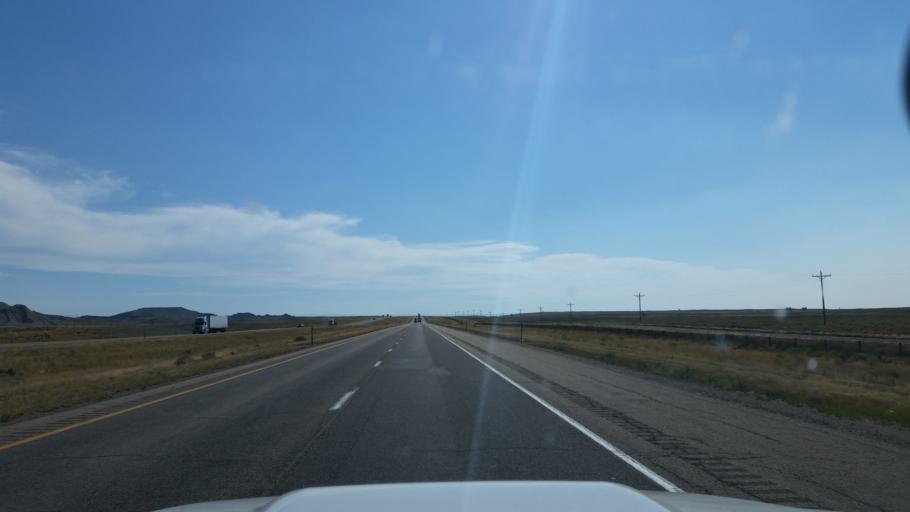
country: US
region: Wyoming
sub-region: Uinta County
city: Lyman
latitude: 41.4456
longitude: -110.0832
